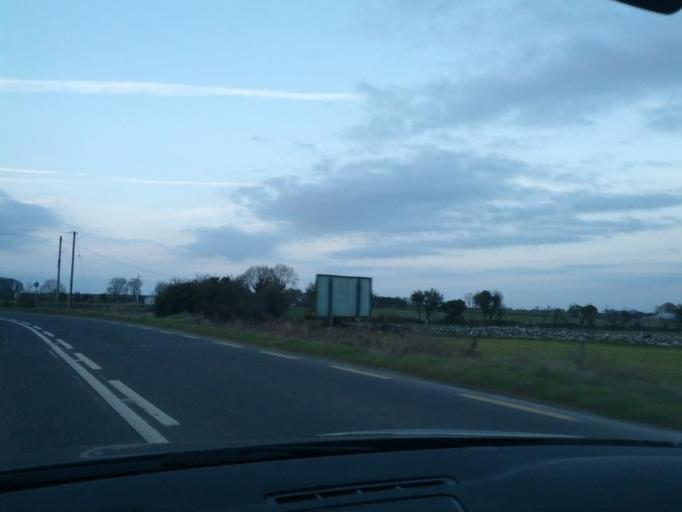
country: IE
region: Connaught
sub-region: County Galway
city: Portumna
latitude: 53.0199
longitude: -8.1256
